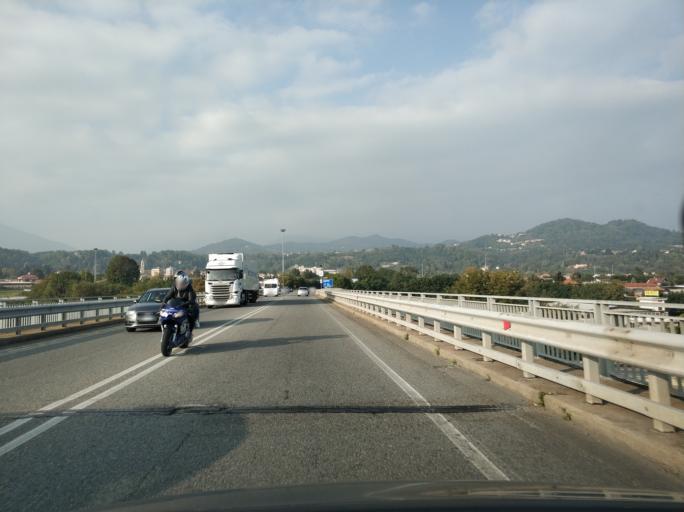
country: IT
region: Piedmont
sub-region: Provincia di Biella
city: Biella
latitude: 45.5609
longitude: 8.0733
